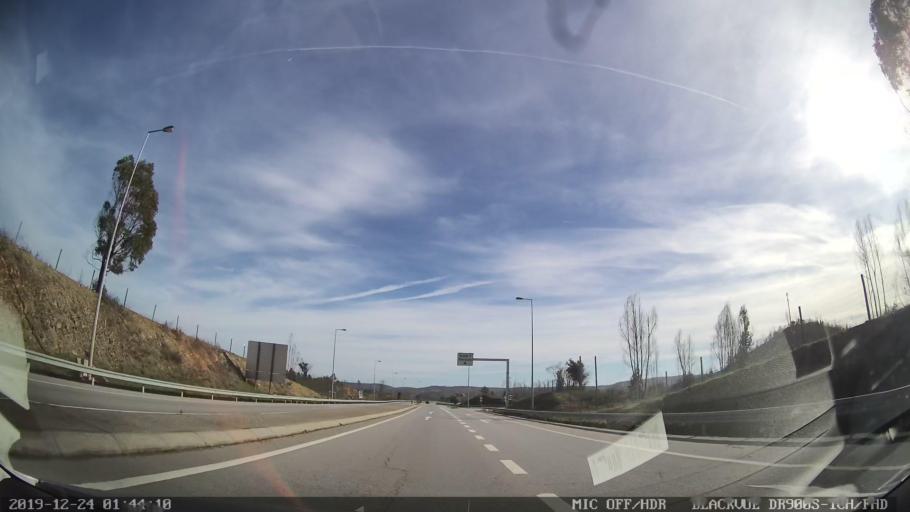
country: PT
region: Portalegre
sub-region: Nisa
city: Nisa
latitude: 39.5567
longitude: -7.7974
